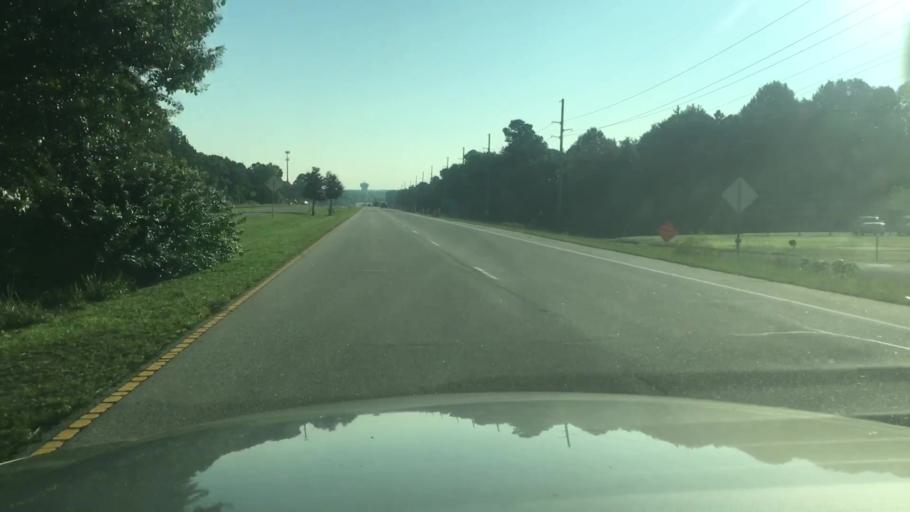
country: US
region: North Carolina
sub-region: Cumberland County
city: Fayetteville
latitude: 35.0230
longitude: -78.8925
